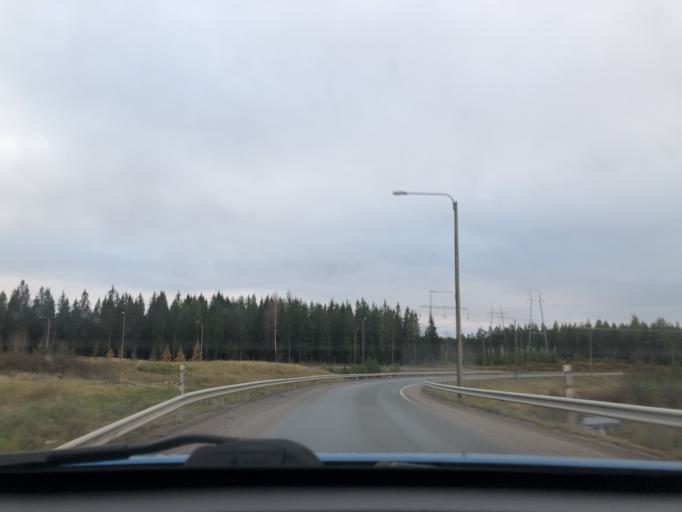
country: FI
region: Pirkanmaa
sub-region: Tampere
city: Kangasala
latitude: 61.5389
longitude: 23.9772
